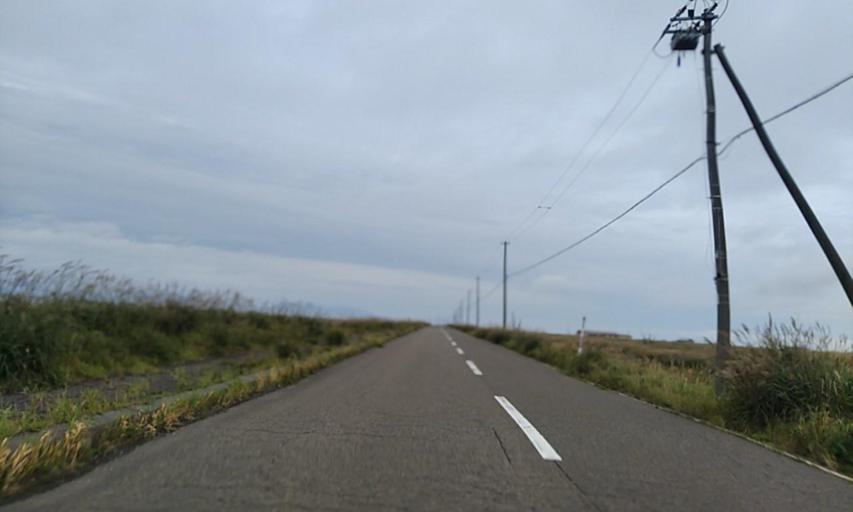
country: JP
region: Hokkaido
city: Shibetsu
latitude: 43.5737
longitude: 145.3440
